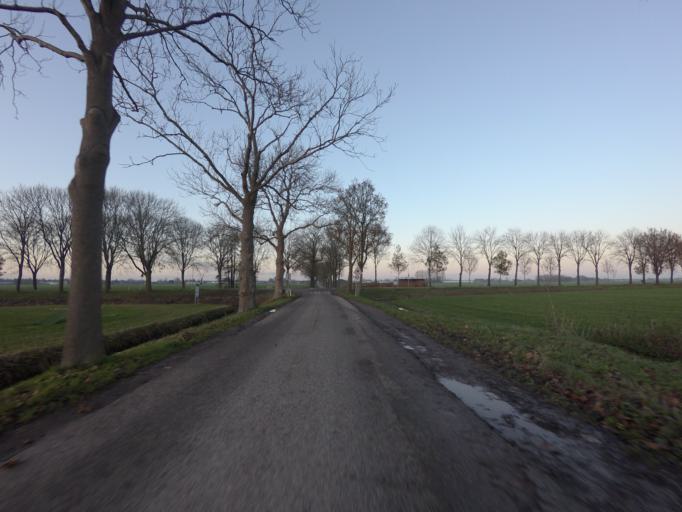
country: NL
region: Gelderland
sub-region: Gemeente Maasdriel
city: Hedel
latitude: 51.7631
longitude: 5.2253
